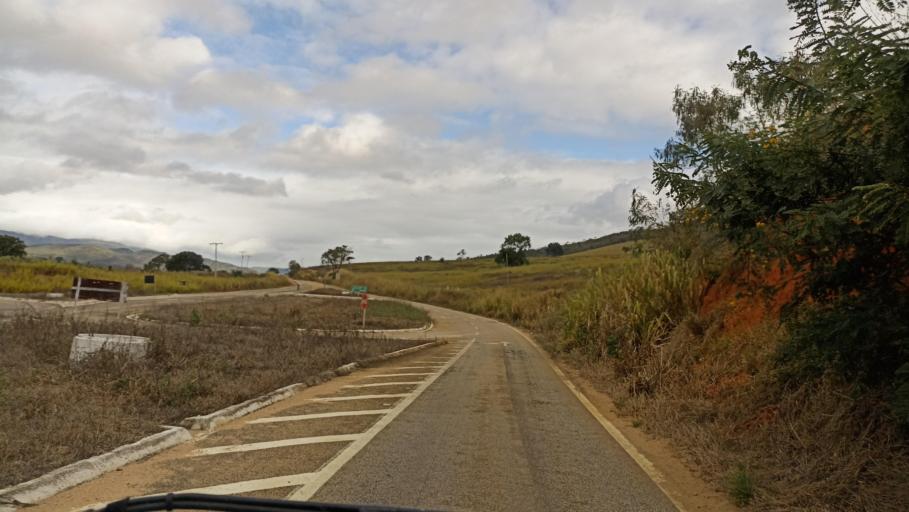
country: BR
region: Minas Gerais
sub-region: Joaima
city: Joaima
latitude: -16.6973
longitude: -40.9549
